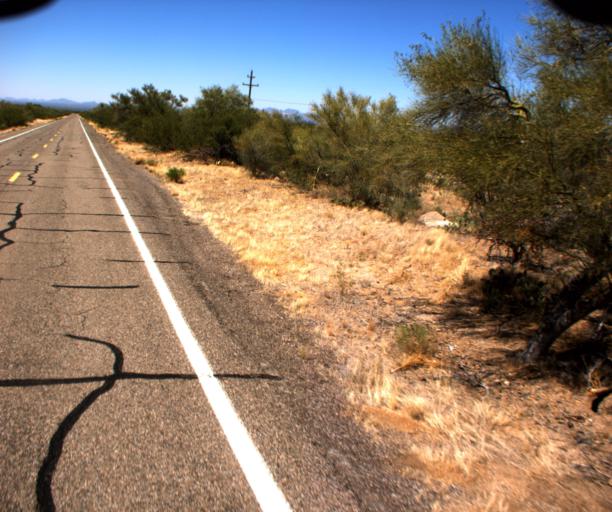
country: US
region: Arizona
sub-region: Pima County
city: Three Points
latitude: 32.0144
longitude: -111.5752
